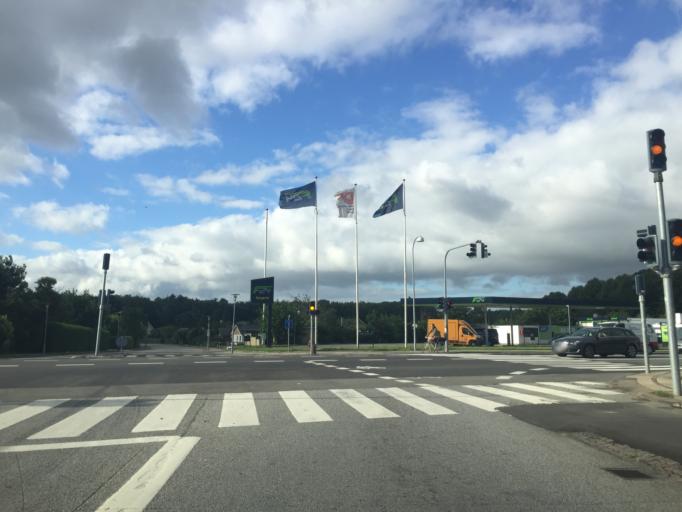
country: DK
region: Capital Region
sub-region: Brondby Kommune
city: Brondbyvester
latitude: 55.6547
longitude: 12.4285
